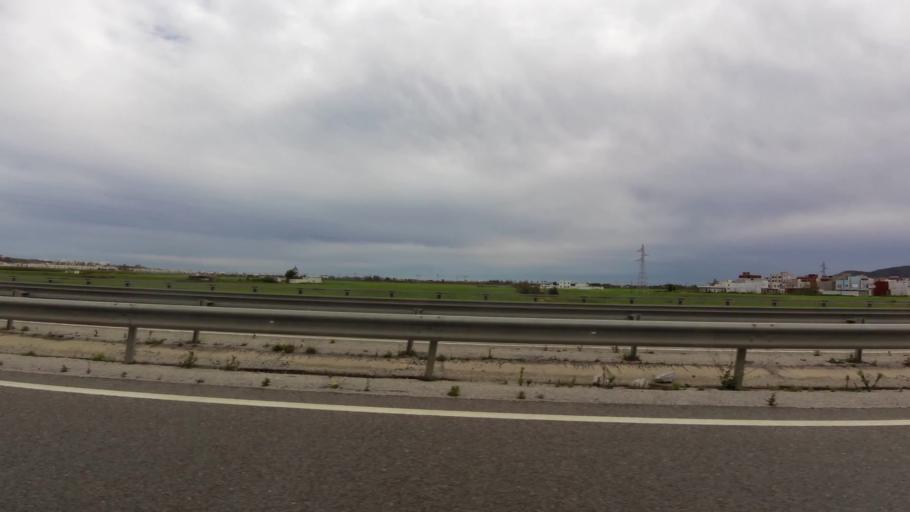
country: MA
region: Tanger-Tetouan
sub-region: Tetouan
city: Martil
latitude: 35.7044
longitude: -5.3546
